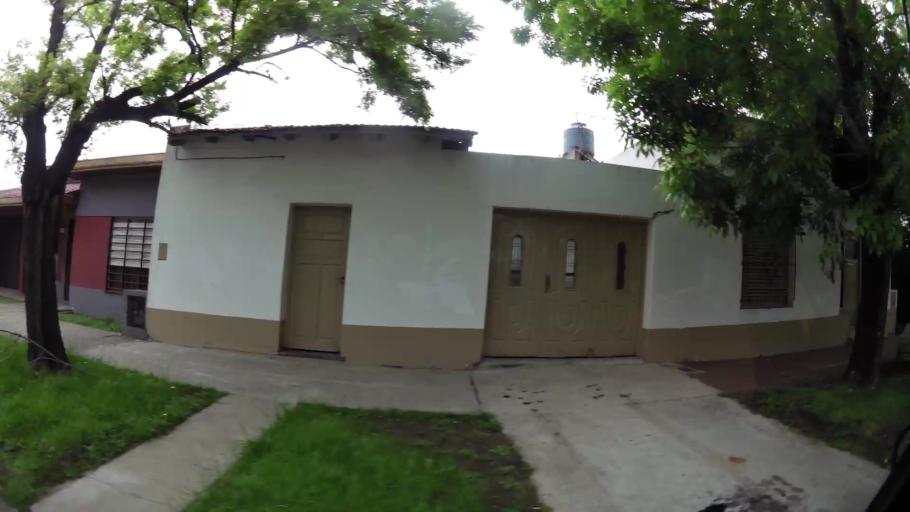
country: AR
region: Buenos Aires
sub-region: Partido de Quilmes
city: Quilmes
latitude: -34.8012
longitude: -58.2732
